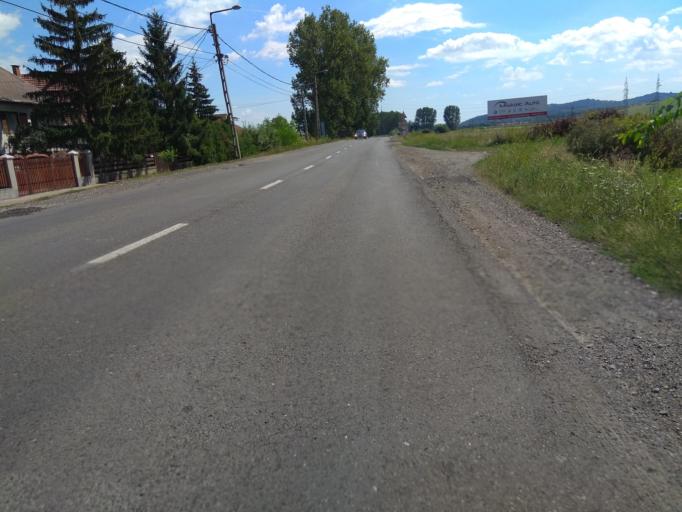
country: HU
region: Borsod-Abauj-Zemplen
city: Sajokaza
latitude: 48.2704
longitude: 20.5885
